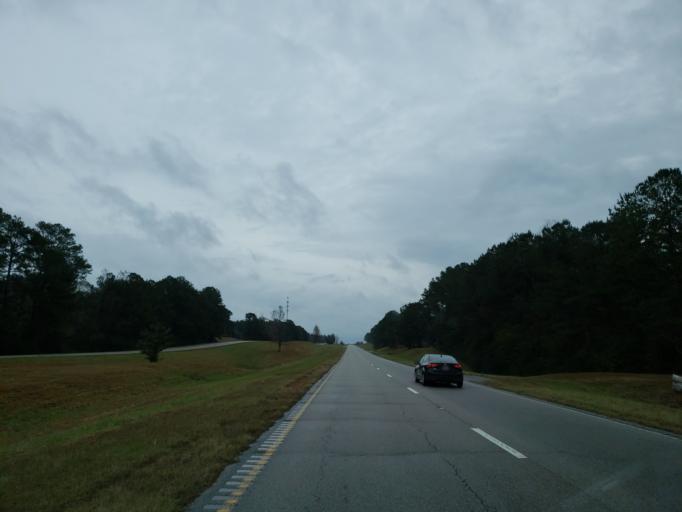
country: US
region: Mississippi
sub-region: Jones County
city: Sharon
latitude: 31.7055
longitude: -88.9319
